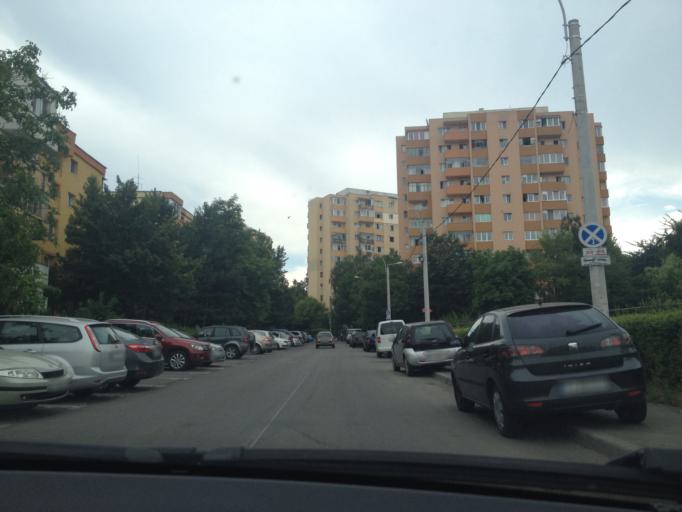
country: RO
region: Cluj
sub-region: Municipiul Cluj-Napoca
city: Cluj-Napoca
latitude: 46.7535
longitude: 23.5518
